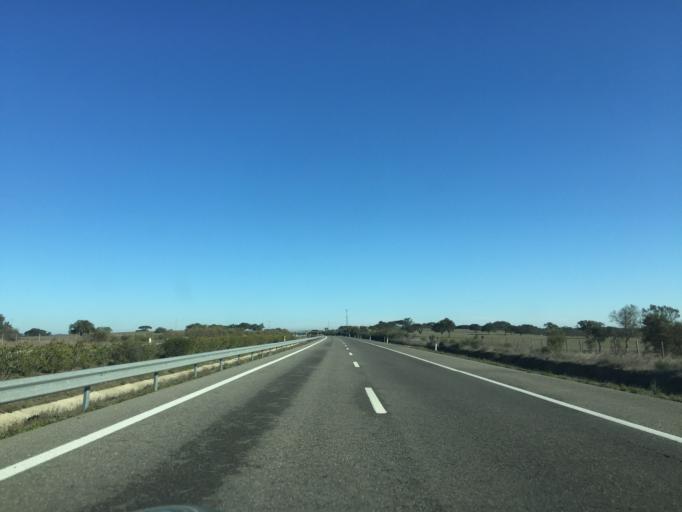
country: PT
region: Beja
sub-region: Ourique
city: Ourique
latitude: 37.6110
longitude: -8.1656
